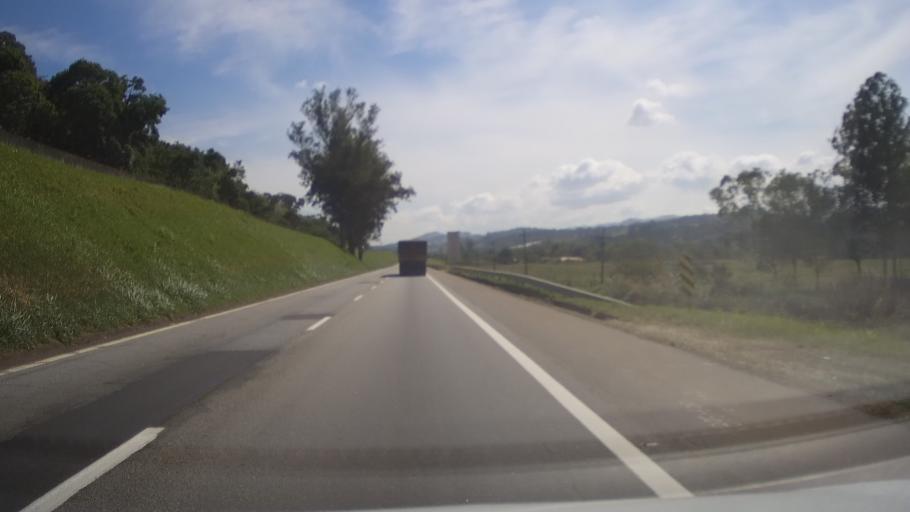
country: BR
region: Minas Gerais
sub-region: Cambui
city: Cambui
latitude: -22.5873
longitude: -46.0502
